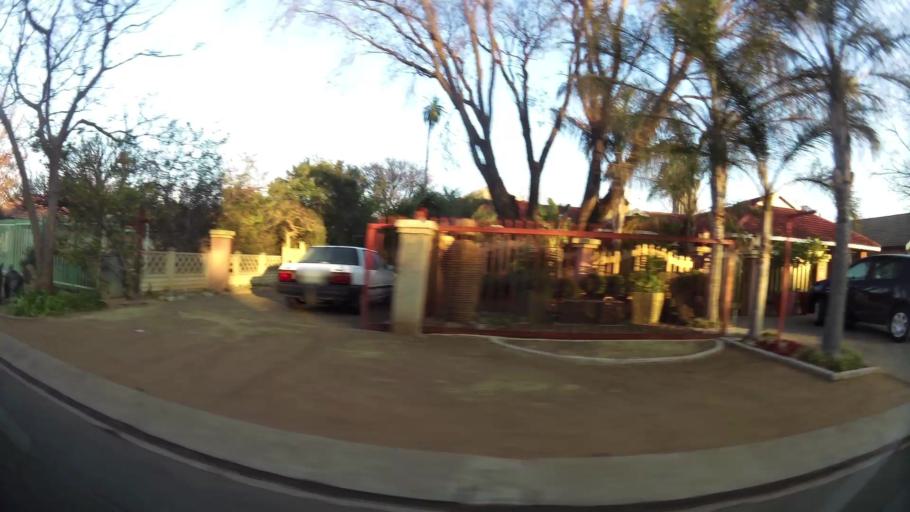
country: ZA
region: Orange Free State
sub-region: Mangaung Metropolitan Municipality
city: Bloemfontein
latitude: -29.1031
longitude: 26.1586
